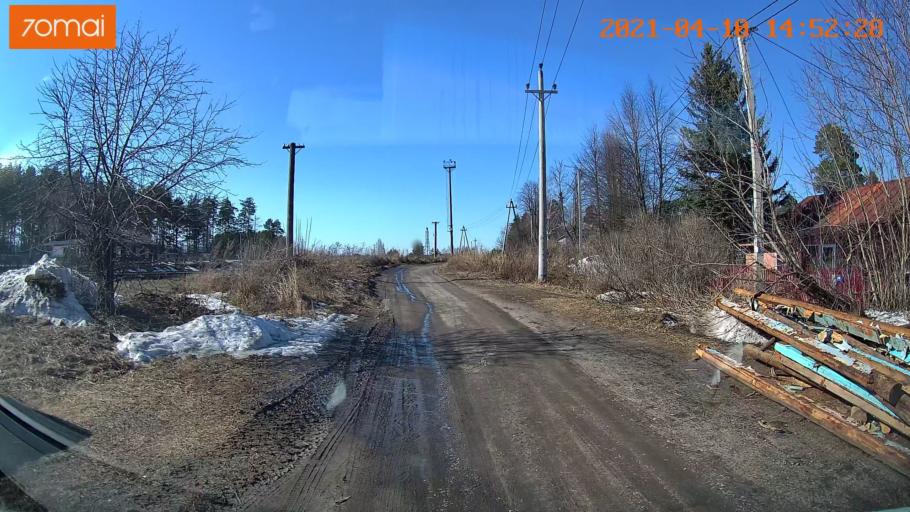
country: RU
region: Ivanovo
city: Kokhma
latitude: 56.9854
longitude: 41.0614
